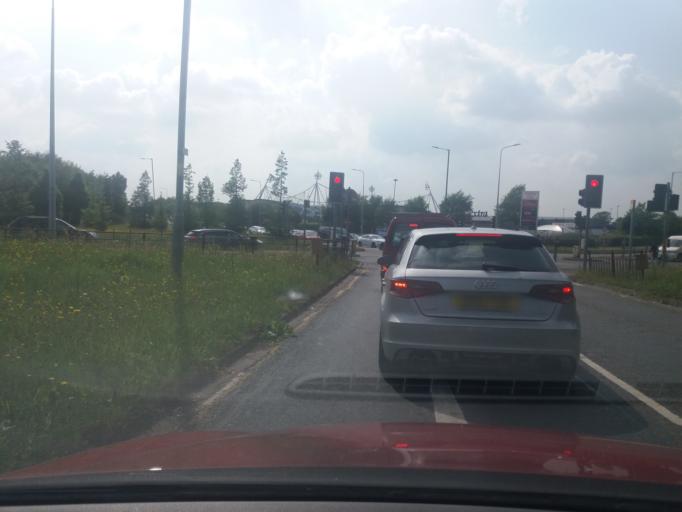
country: GB
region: England
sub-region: Borough of Bolton
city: Horwich
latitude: 53.5815
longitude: -2.5270
